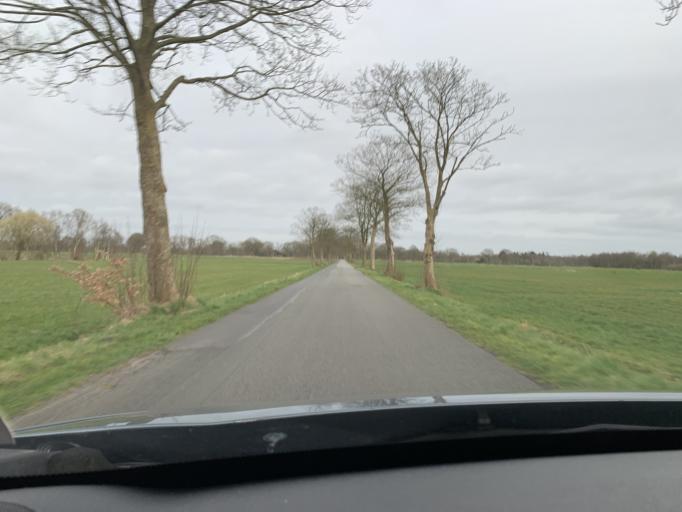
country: DE
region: Lower Saxony
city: Schwerinsdorf
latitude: 53.2699
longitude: 7.7003
